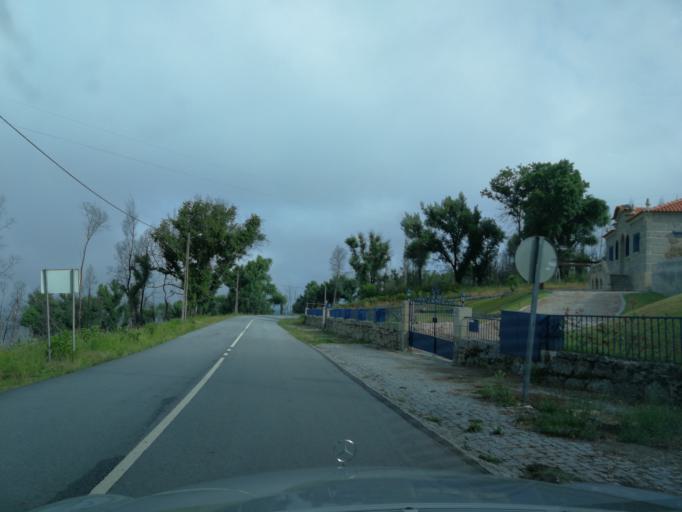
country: PT
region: Braga
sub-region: Braga
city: Braga
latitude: 41.5452
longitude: -8.3730
